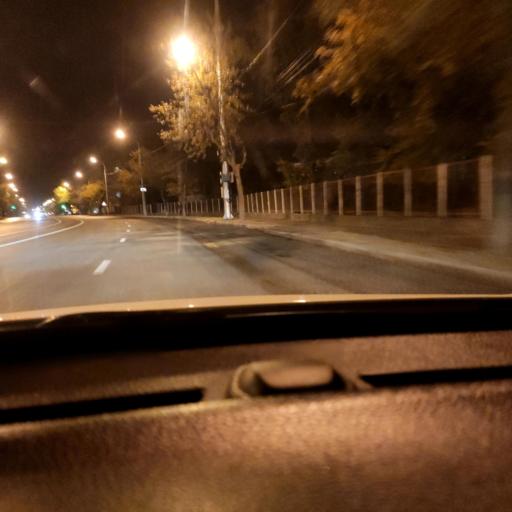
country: RU
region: Voronezj
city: Maslovka
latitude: 51.6150
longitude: 39.2473
